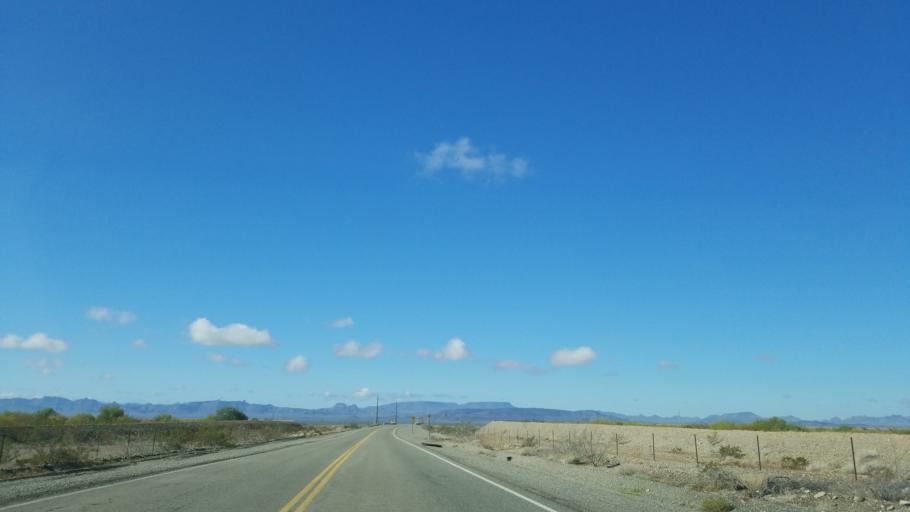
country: US
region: Arizona
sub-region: La Paz County
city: Salome
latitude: 33.7414
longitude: -113.7542
